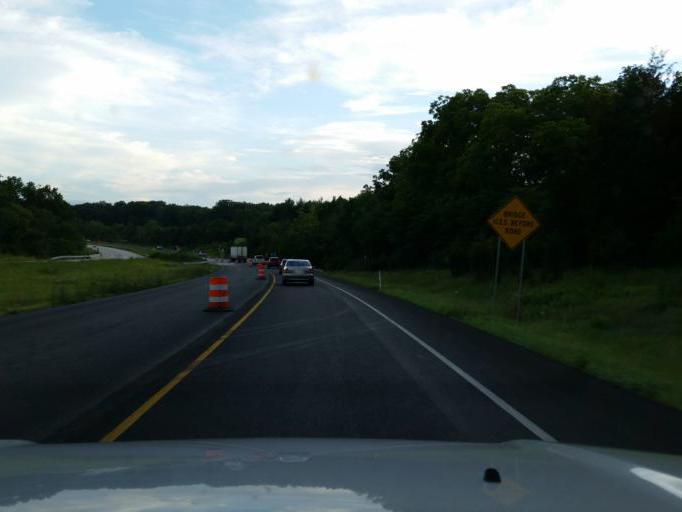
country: US
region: Maryland
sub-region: Frederick County
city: Emmitsburg
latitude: 39.7369
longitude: -77.2955
